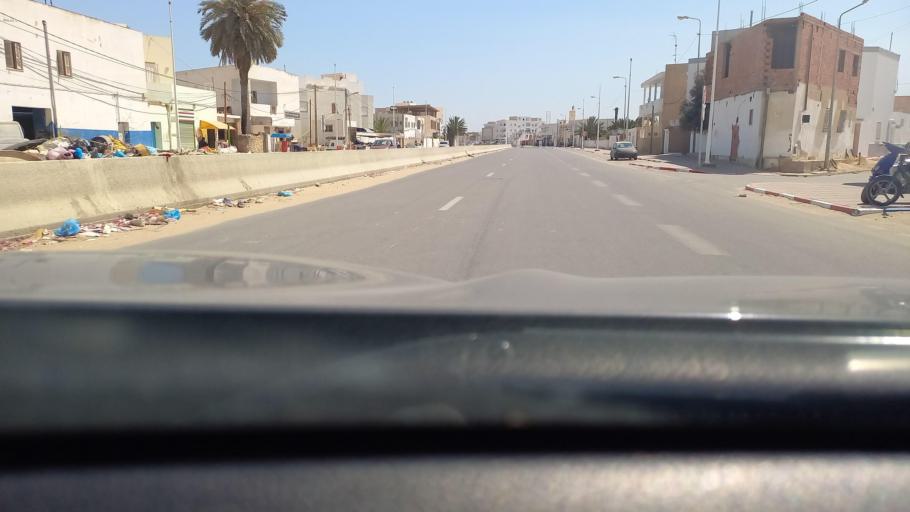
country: TN
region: Safaqis
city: Sfax
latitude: 34.7433
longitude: 10.7247
